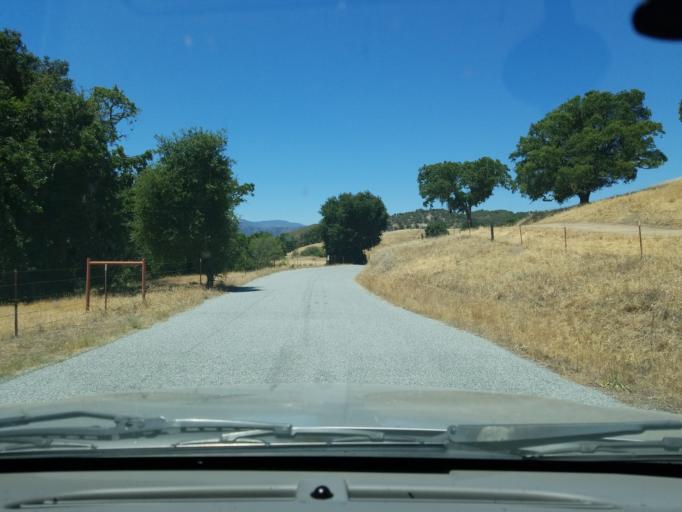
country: US
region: California
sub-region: Monterey County
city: Gonzales
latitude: 36.3944
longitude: -121.5709
